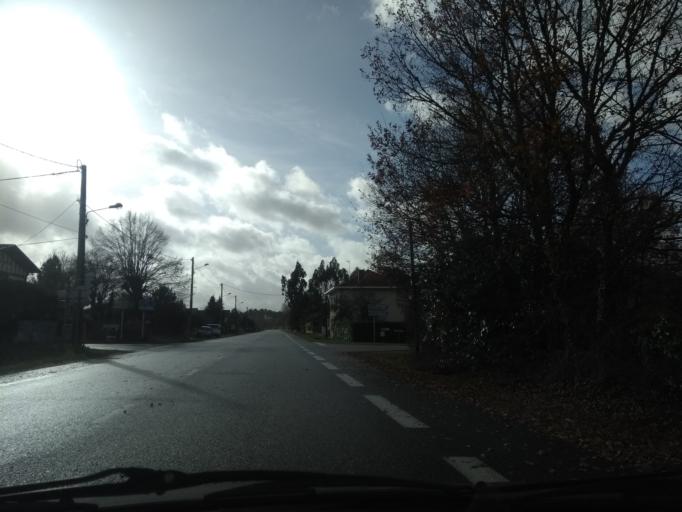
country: FR
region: Aquitaine
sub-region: Departement de la Gironde
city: Belin-Beliet
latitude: 44.4894
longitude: -0.7915
